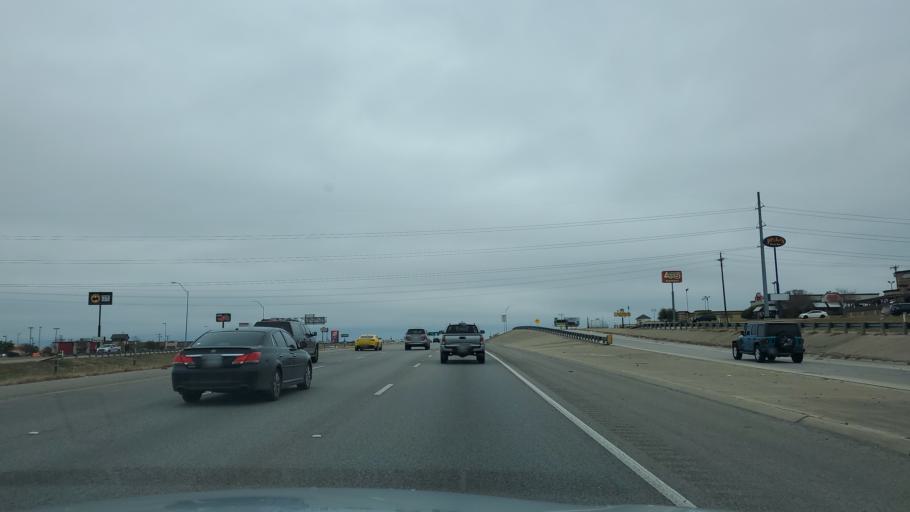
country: US
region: Texas
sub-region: Bell County
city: Killeen
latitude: 31.0882
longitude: -97.7147
